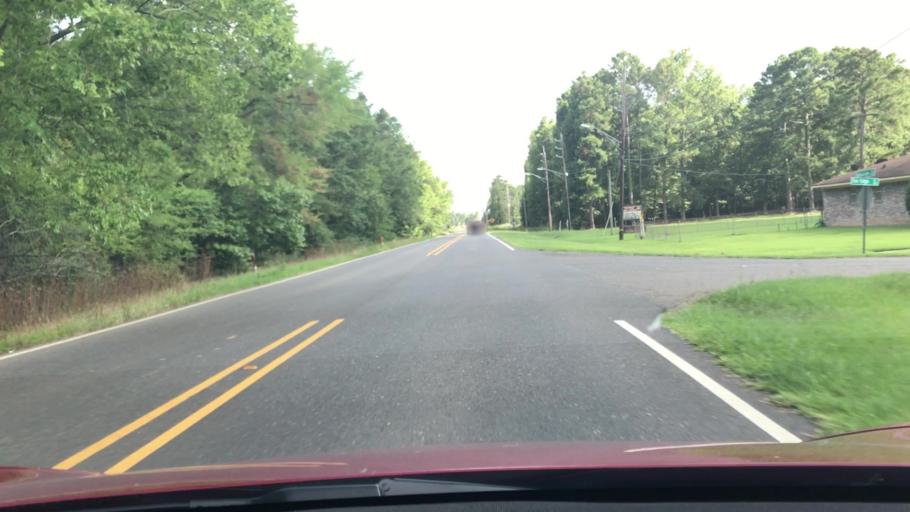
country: US
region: Louisiana
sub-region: Bossier Parish
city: Bossier City
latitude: 32.3938
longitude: -93.7386
